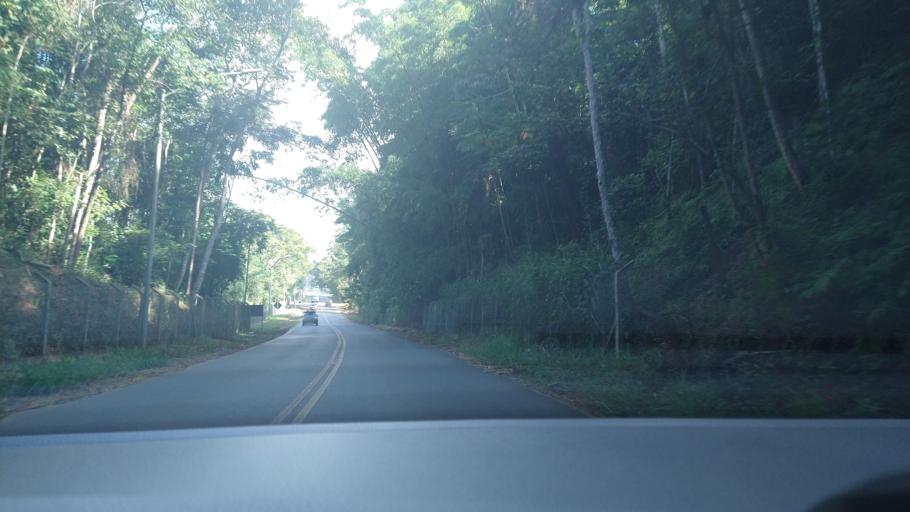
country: BR
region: Minas Gerais
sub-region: Vicosa
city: Vicosa
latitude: -20.7687
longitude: -42.8739
